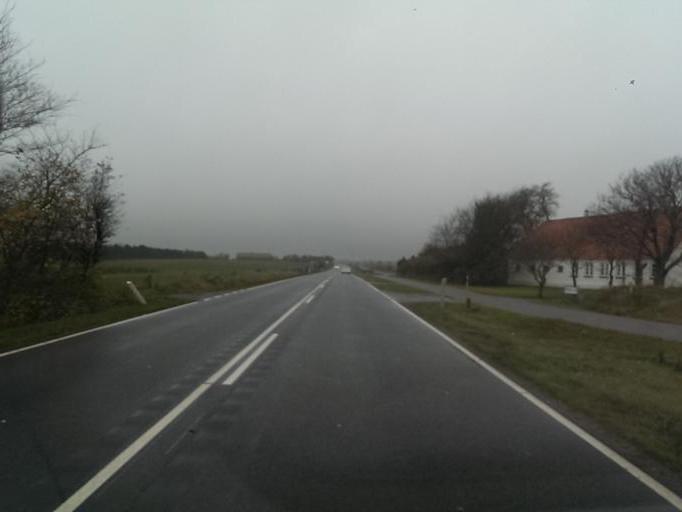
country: DK
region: South Denmark
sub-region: Esbjerg Kommune
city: Tjaereborg
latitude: 55.4632
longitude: 8.5555
